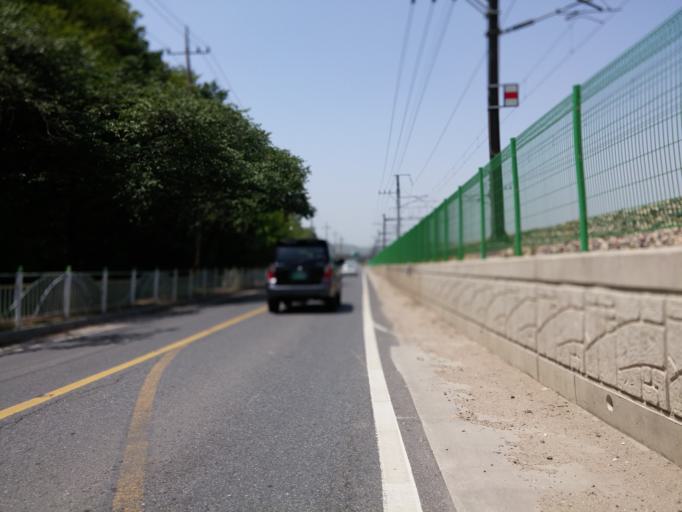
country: KR
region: Chungcheongnam-do
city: Nonsan
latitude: 36.2155
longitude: 127.2113
